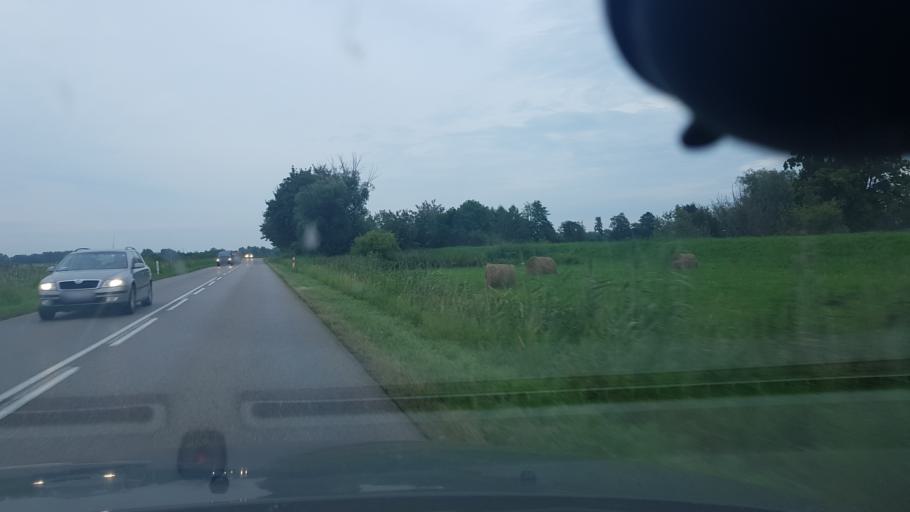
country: PL
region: Pomeranian Voivodeship
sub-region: Powiat nowodworski
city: Nowy Dwor Gdanski
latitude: 54.2386
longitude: 19.1316
